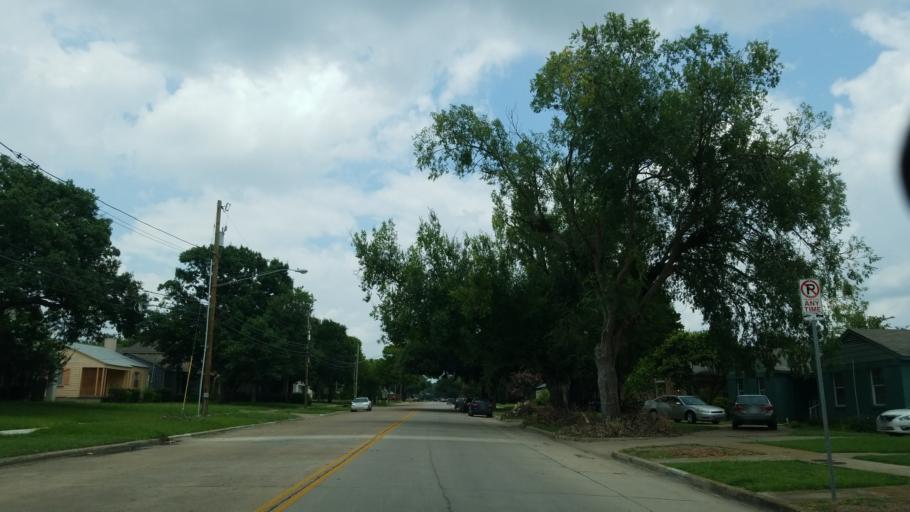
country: US
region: Texas
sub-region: Dallas County
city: University Park
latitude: 32.8450
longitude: -96.8274
